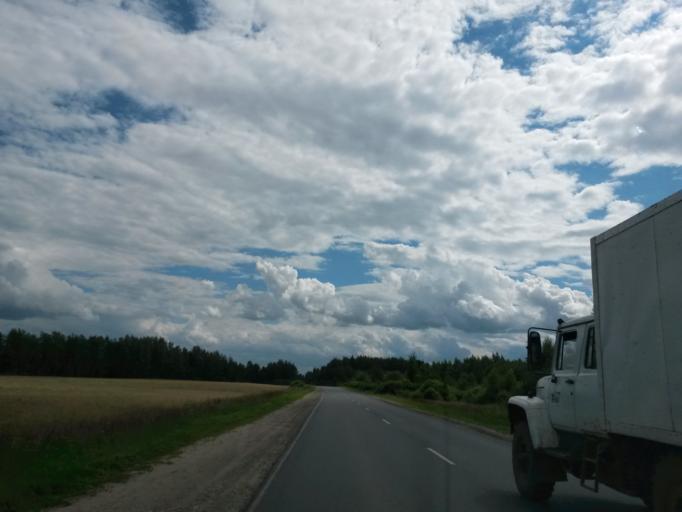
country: RU
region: Ivanovo
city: Novo-Talitsy
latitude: 57.0346
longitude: 40.7481
